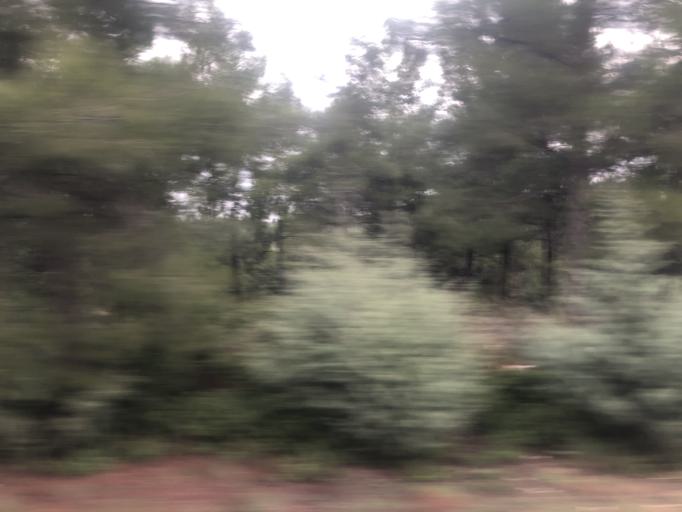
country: TR
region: Izmir
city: Buca
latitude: 38.3683
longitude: 27.2166
